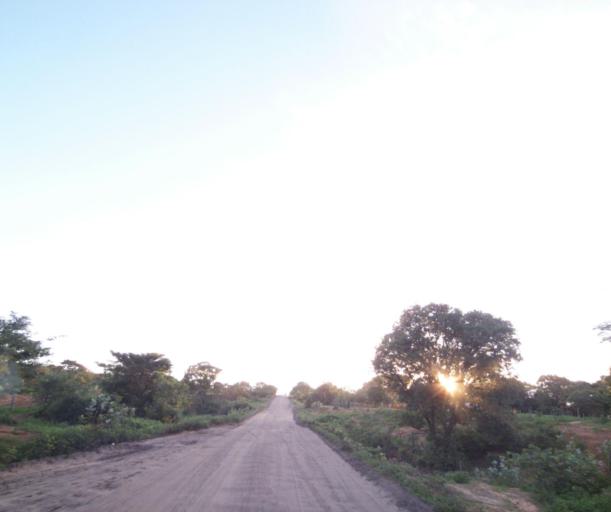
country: BR
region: Bahia
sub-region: Sao Felix Do Coribe
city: Santa Maria da Vitoria
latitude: -13.6234
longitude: -44.4179
